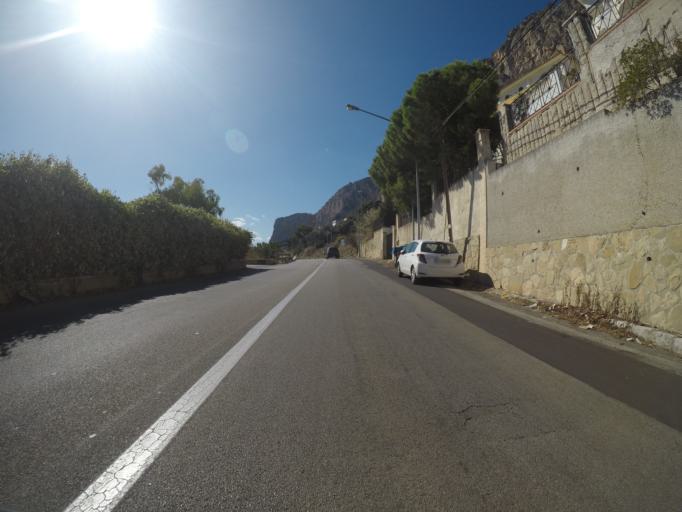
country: IT
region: Sicily
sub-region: Palermo
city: Palermo
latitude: 38.1778
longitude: 13.3661
